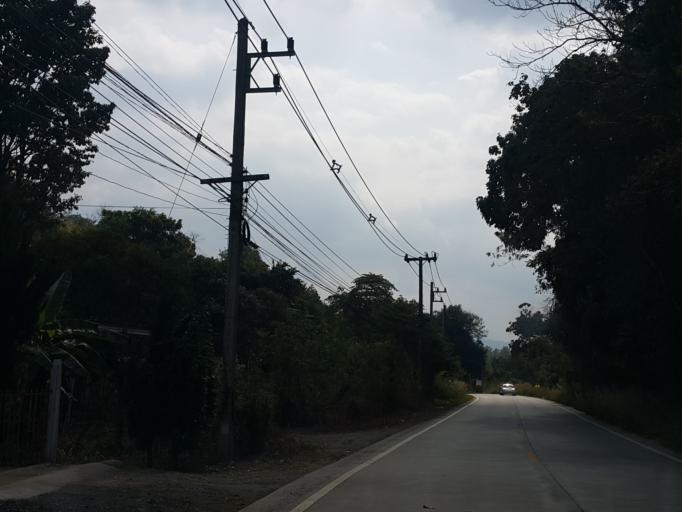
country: TH
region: Chiang Mai
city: Mae On
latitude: 18.8020
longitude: 99.2393
